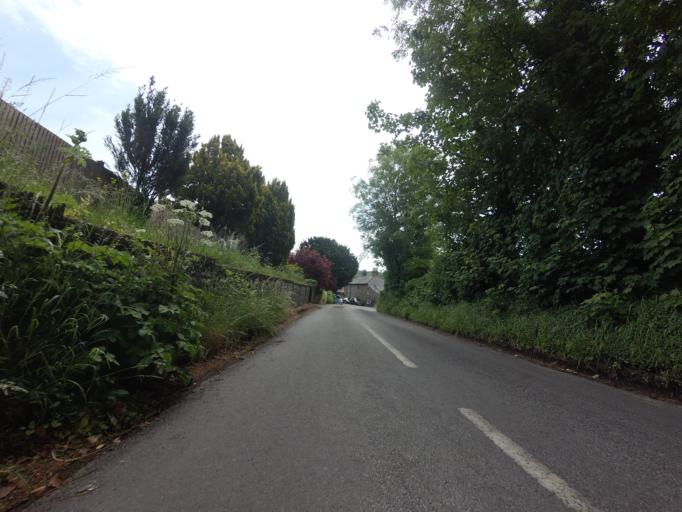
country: GB
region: England
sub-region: Kent
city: Shoreham
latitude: 51.3385
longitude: 0.1779
